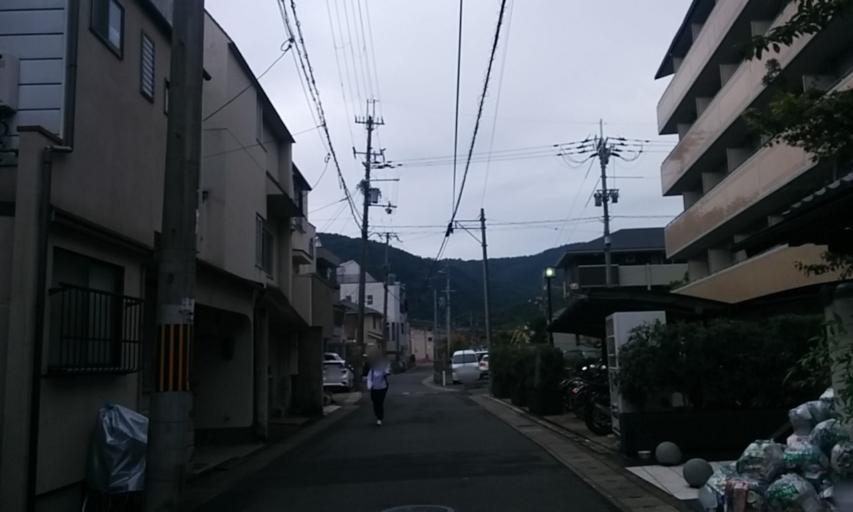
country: JP
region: Kyoto
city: Muko
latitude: 35.0193
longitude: 135.6807
